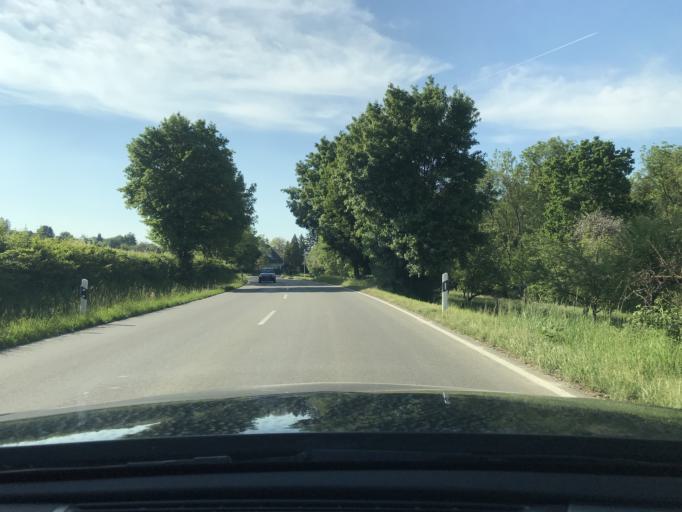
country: DE
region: Baden-Wuerttemberg
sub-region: Regierungsbezirk Stuttgart
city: Schwaikheim
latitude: 48.8819
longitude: 9.3170
